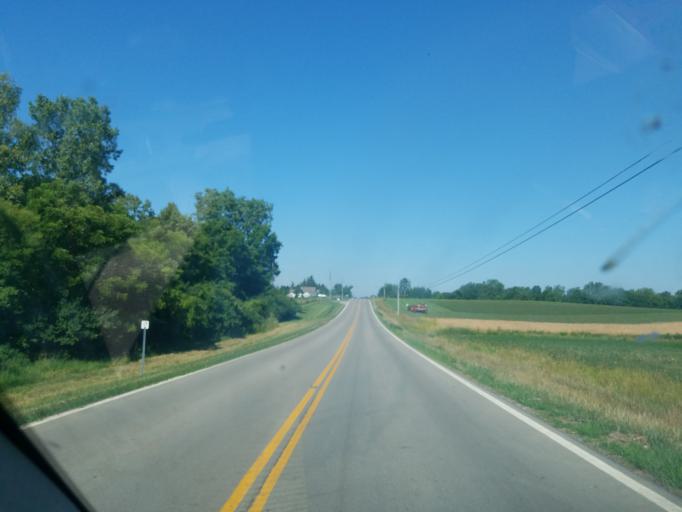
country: US
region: Ohio
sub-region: Logan County
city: Northwood
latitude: 40.4576
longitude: -83.7008
